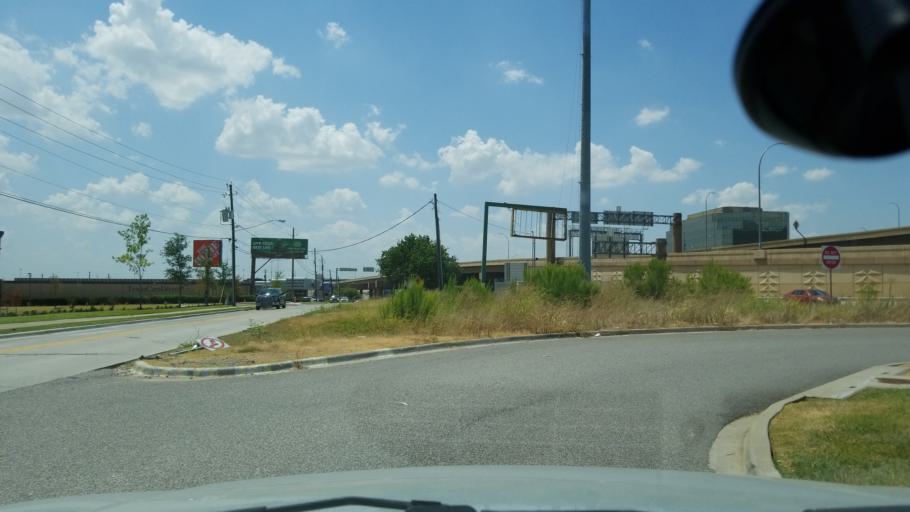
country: US
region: Texas
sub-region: Dallas County
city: Farmers Branch
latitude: 32.9094
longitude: -96.8840
